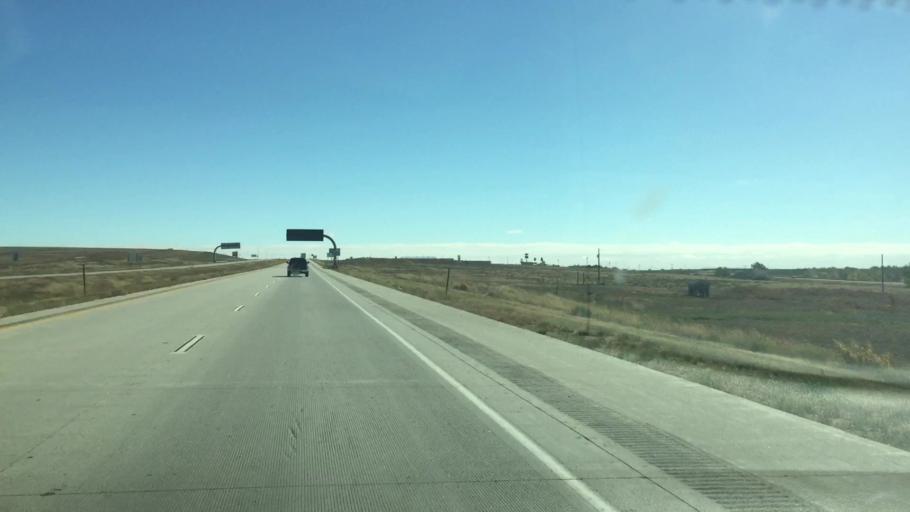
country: US
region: Colorado
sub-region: Lincoln County
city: Limon
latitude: 39.2731
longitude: -103.7287
